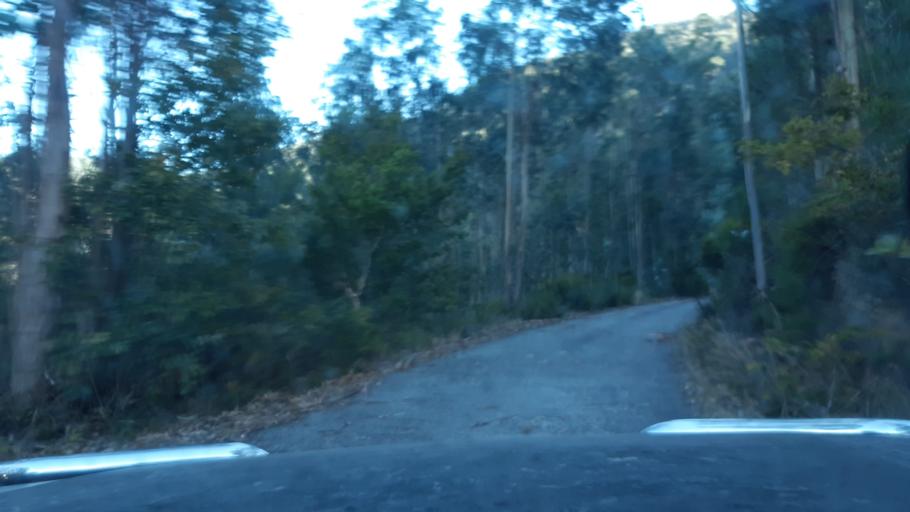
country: PT
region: Viseu
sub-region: Mortagua
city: Mortagua
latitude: 40.5228
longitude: -8.2524
